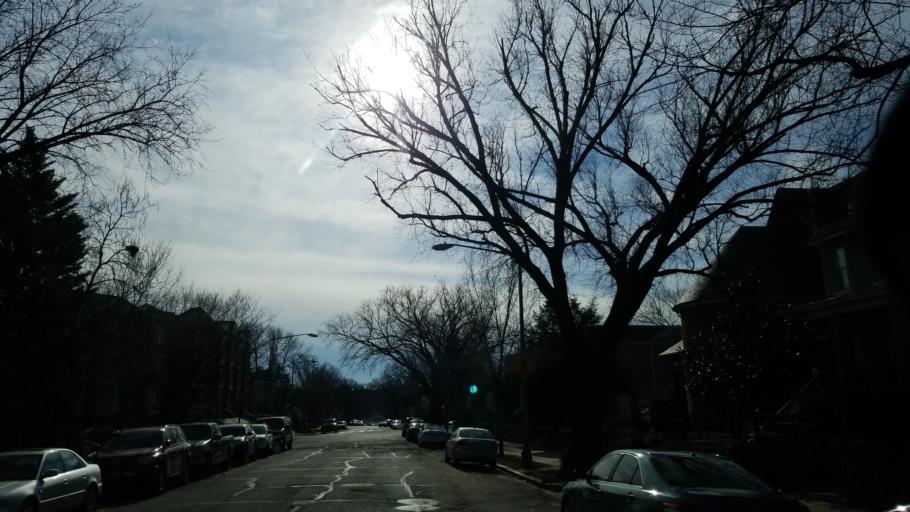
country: US
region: Washington, D.C.
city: Washington, D.C.
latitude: 38.8825
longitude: -76.9842
